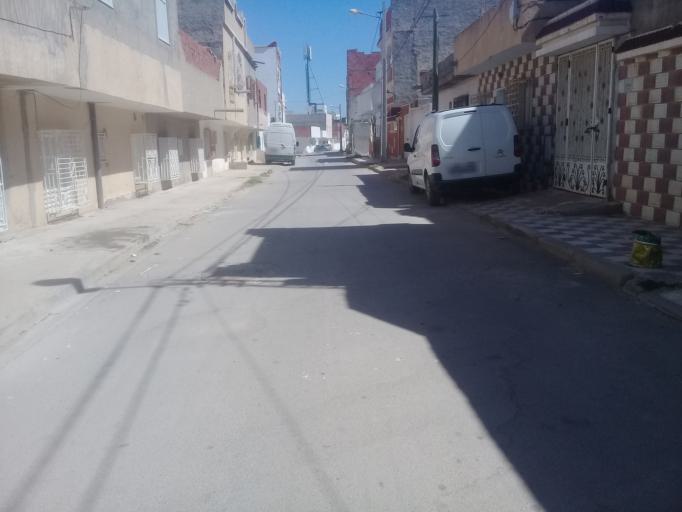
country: TN
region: Al Qayrawan
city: Kairouan
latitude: 35.6592
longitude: 10.1071
